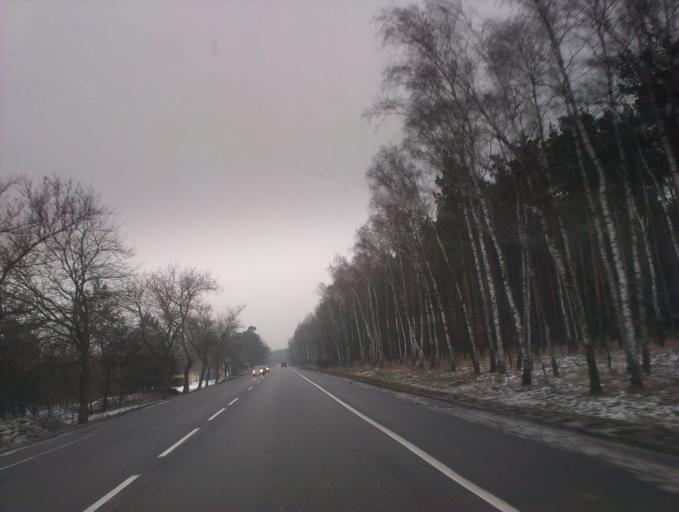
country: PL
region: Greater Poland Voivodeship
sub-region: Powiat obornicki
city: Oborniki
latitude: 52.6967
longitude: 16.8939
